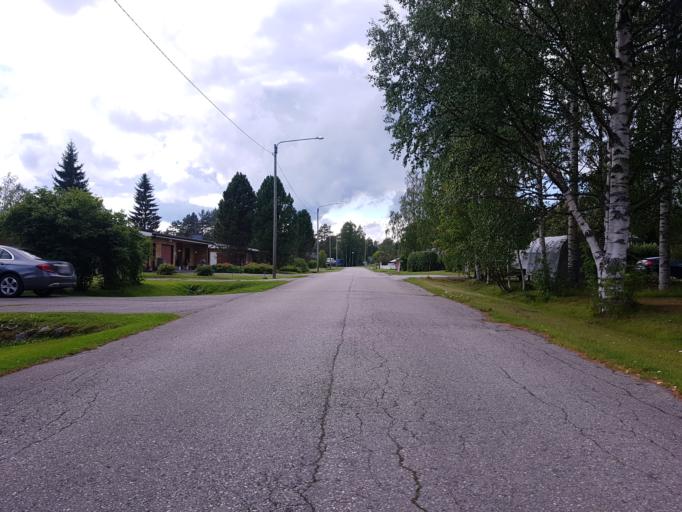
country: FI
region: Kainuu
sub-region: Kehys-Kainuu
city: Kuhmo
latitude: 64.1243
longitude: 29.5414
